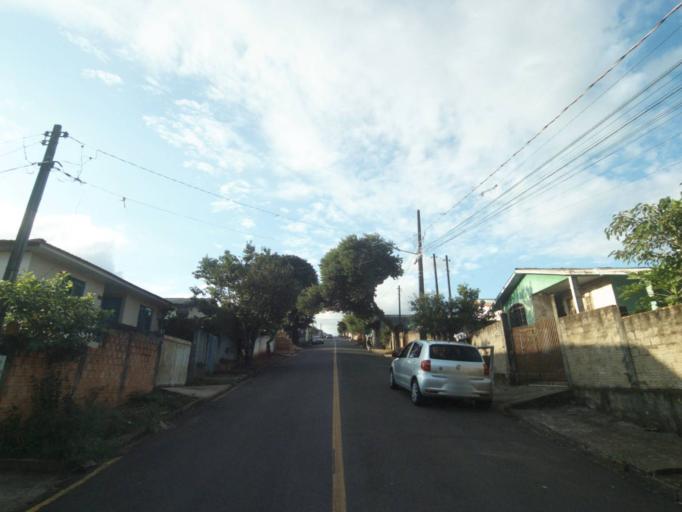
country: BR
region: Parana
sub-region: Telemaco Borba
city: Telemaco Borba
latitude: -24.3252
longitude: -50.6390
